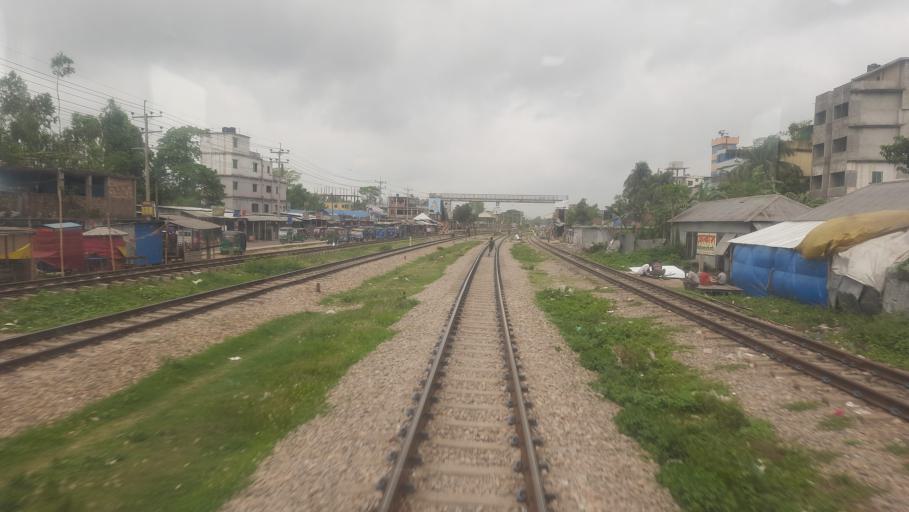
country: BD
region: Dhaka
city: Narsingdi
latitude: 23.9362
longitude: 90.7737
